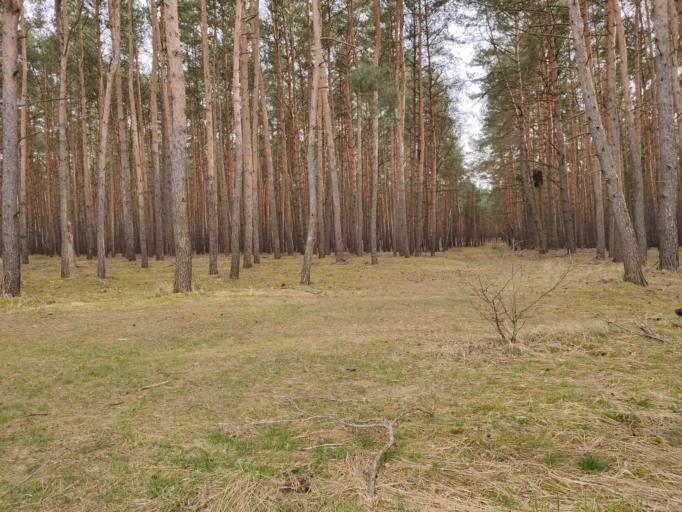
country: PL
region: Greater Poland Voivodeship
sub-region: Powiat sredzki
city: Sroda Wielkopolska
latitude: 52.1474
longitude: 17.2800
